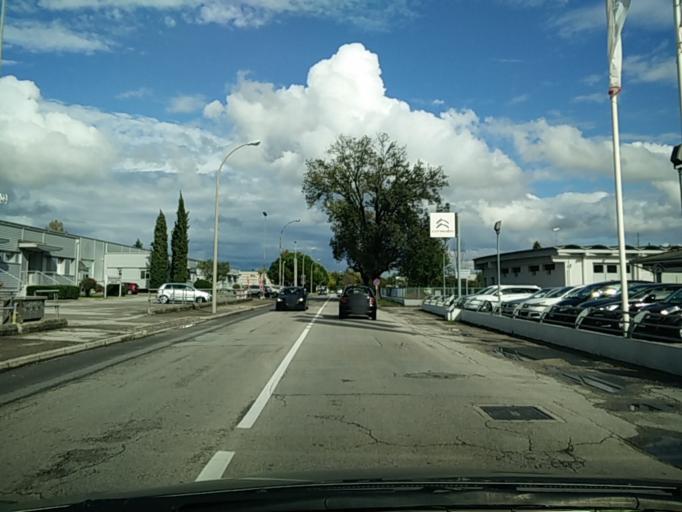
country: IT
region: Veneto
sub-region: Provincia di Treviso
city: San Vendemiano-Fossamerlo
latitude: 45.8900
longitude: 12.3182
